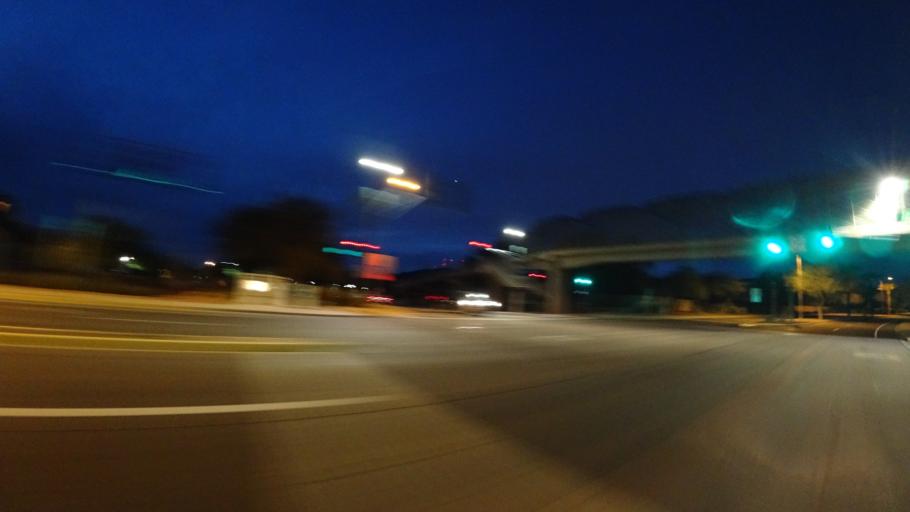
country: US
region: Arizona
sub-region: Maricopa County
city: Guadalupe
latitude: 33.3087
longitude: -112.0274
